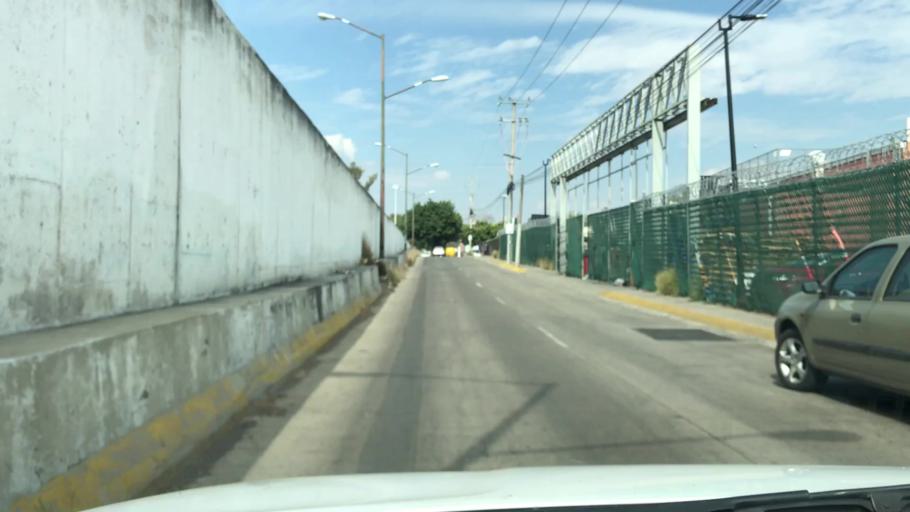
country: MX
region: Jalisco
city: Guadalajara
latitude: 20.6795
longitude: -103.4339
